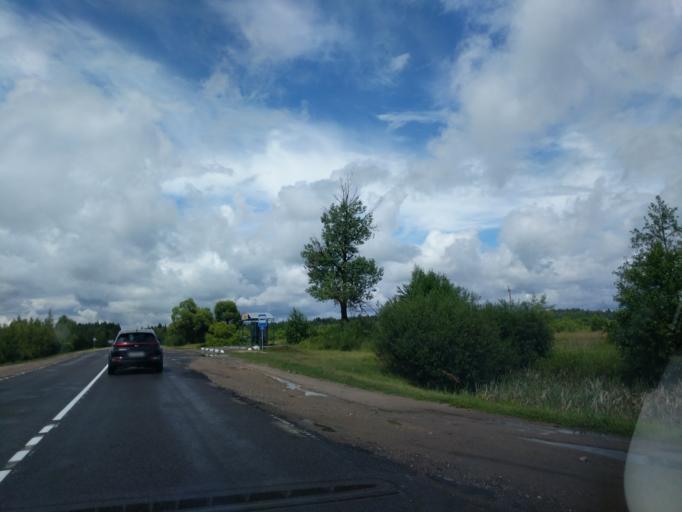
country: BY
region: Minsk
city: Il'ya
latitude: 54.3977
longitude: 27.3342
